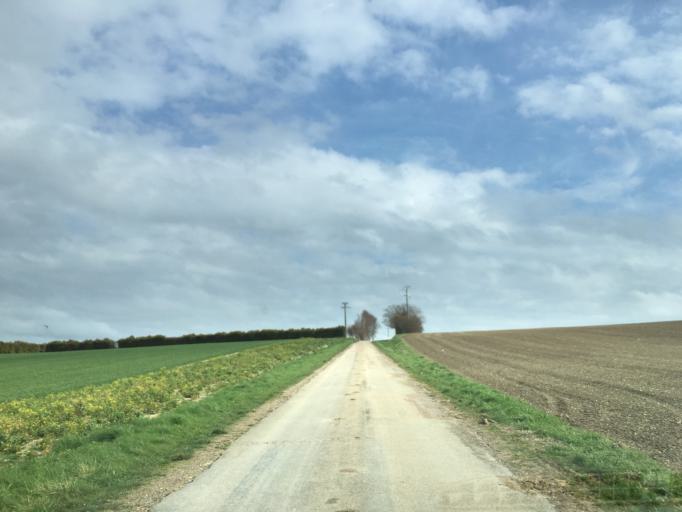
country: FR
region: Bourgogne
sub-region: Departement de l'Yonne
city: Pourrain
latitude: 47.7954
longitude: 3.4134
